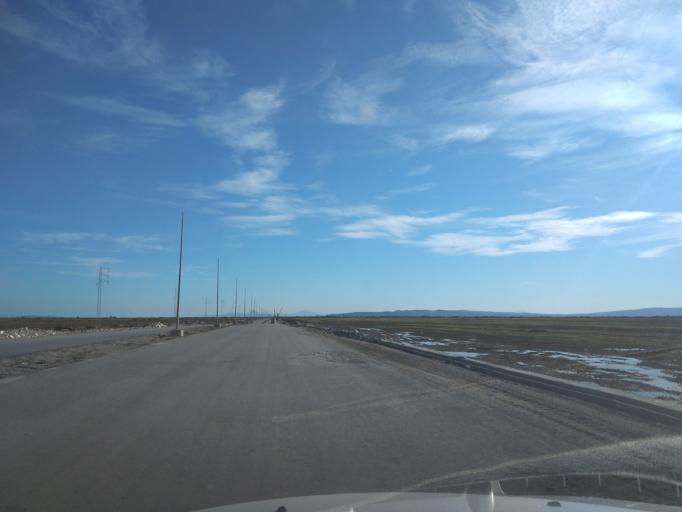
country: TN
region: Ariana
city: Qal'at al Andalus
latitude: 37.0366
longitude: 10.1337
